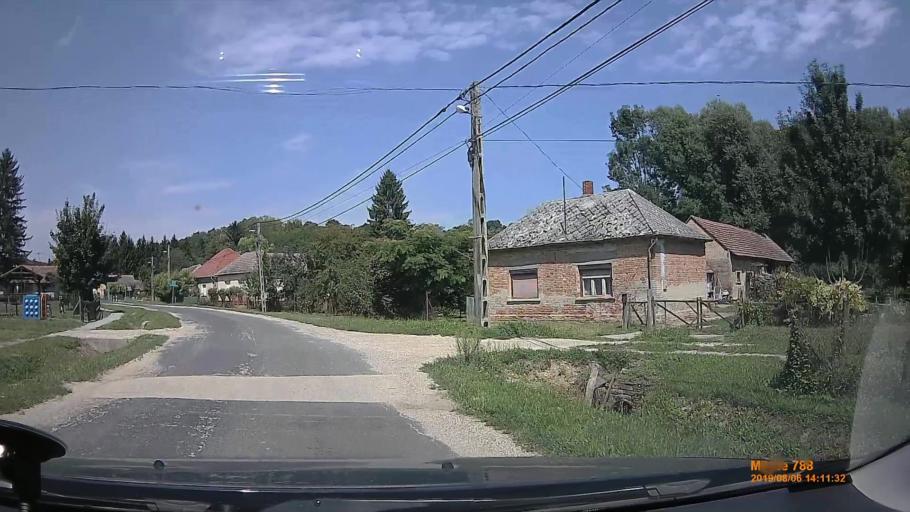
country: HU
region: Zala
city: Zalakomar
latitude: 46.5572
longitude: 17.0791
